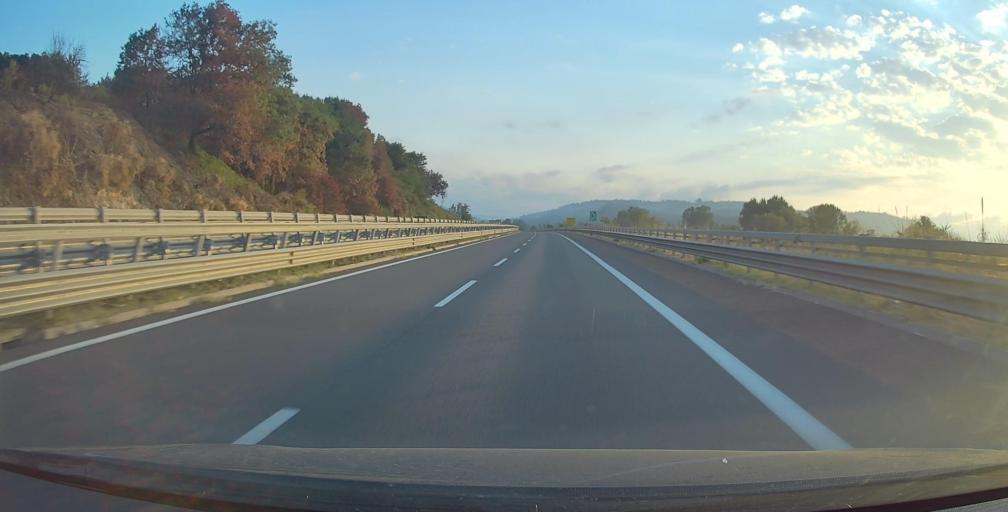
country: IT
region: Calabria
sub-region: Provincia di Reggio Calabria
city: Candidoni
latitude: 38.5161
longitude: 16.0505
